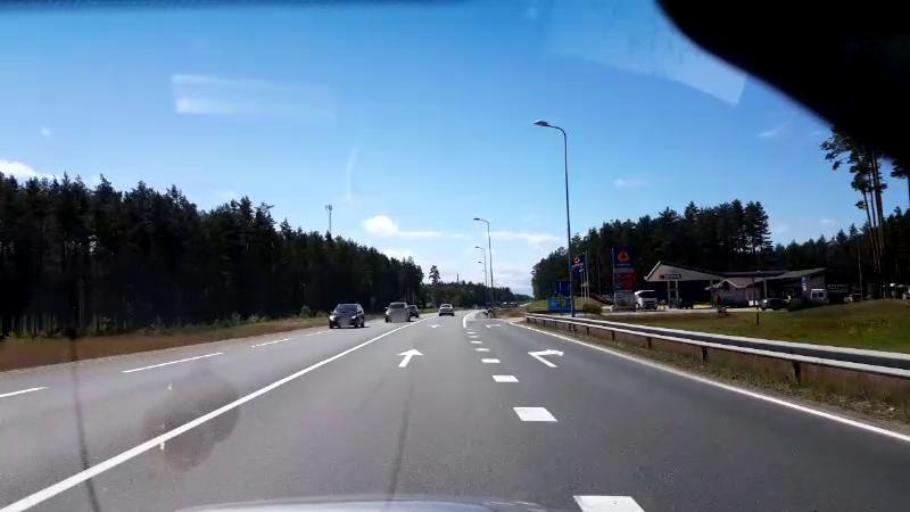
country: LV
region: Saulkrastu
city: Saulkrasti
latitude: 57.2283
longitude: 24.4209
